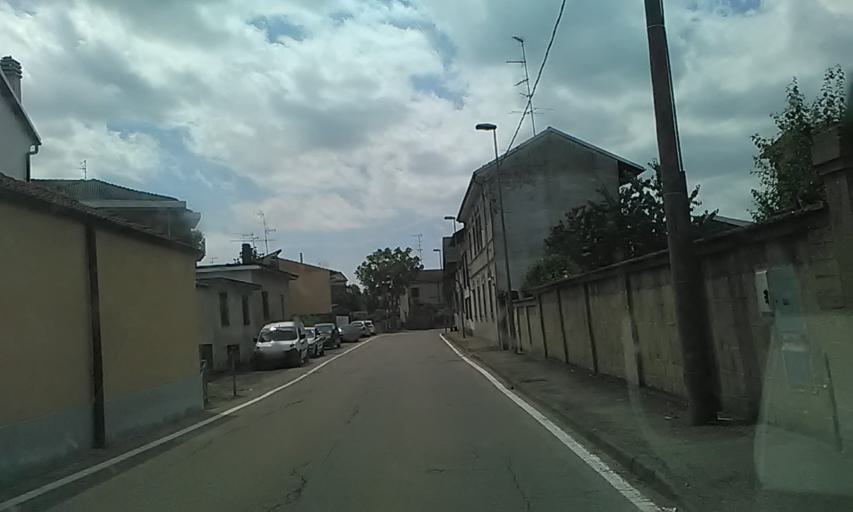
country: IT
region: Piedmont
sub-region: Provincia di Vercelli
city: Vercelli
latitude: 45.3051
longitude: 8.4447
